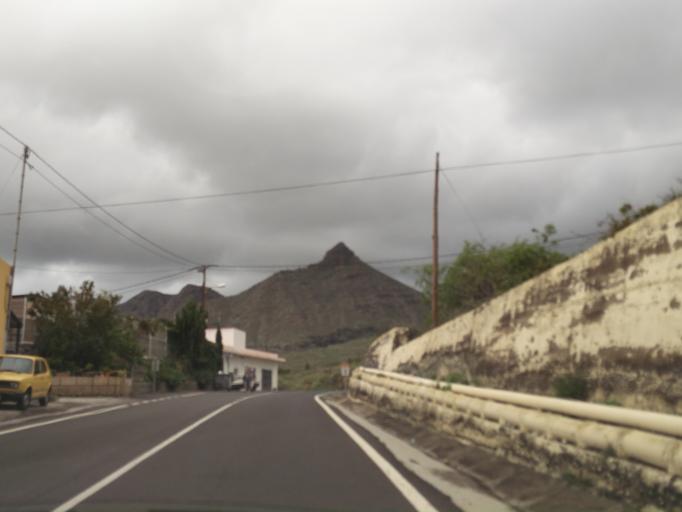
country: ES
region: Canary Islands
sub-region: Provincia de Santa Cruz de Tenerife
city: Arona
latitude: 28.1046
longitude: -16.6844
